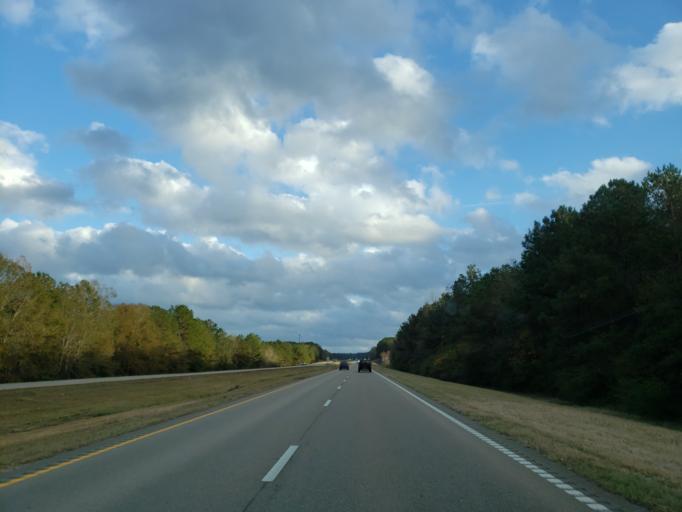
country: US
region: Mississippi
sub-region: Perry County
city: New Augusta
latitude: 31.1652
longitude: -88.9340
